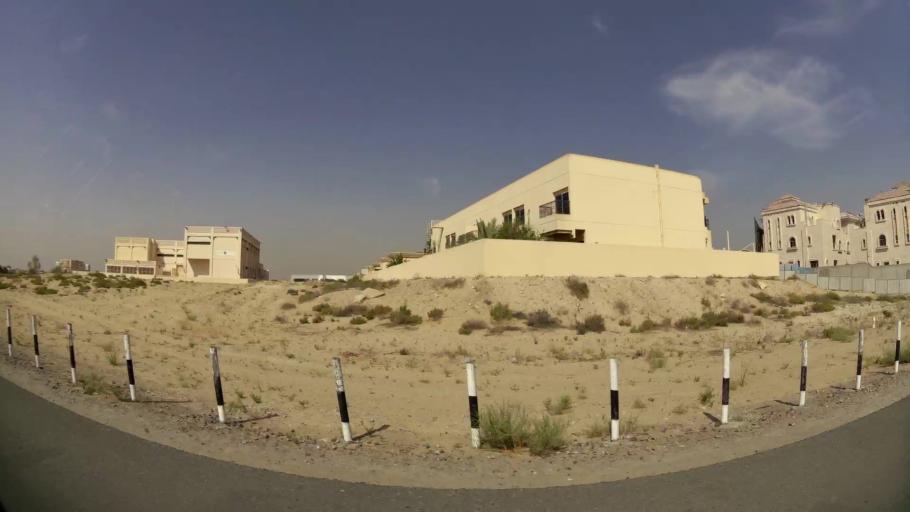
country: AE
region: Ash Shariqah
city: Sharjah
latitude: 25.2172
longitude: 55.4269
